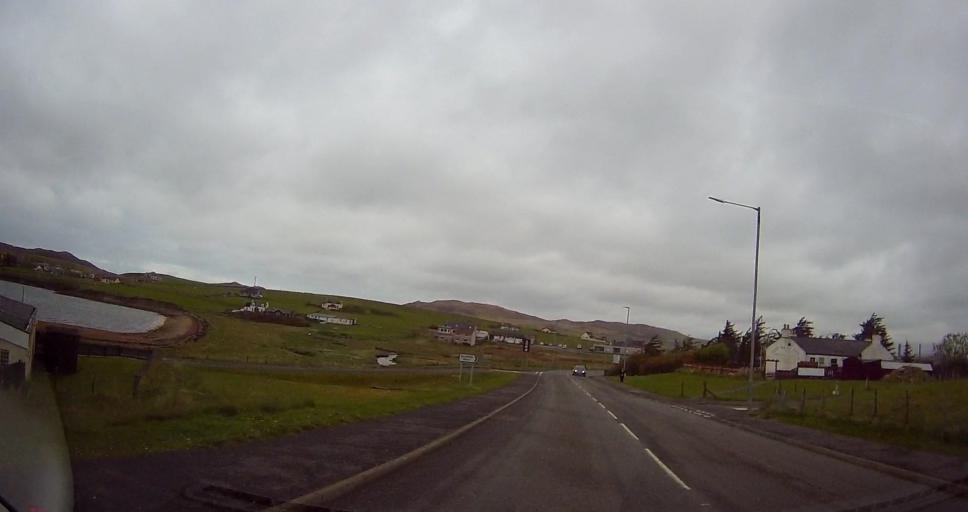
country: GB
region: Scotland
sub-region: Shetland Islands
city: Lerwick
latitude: 60.3938
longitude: -1.3510
